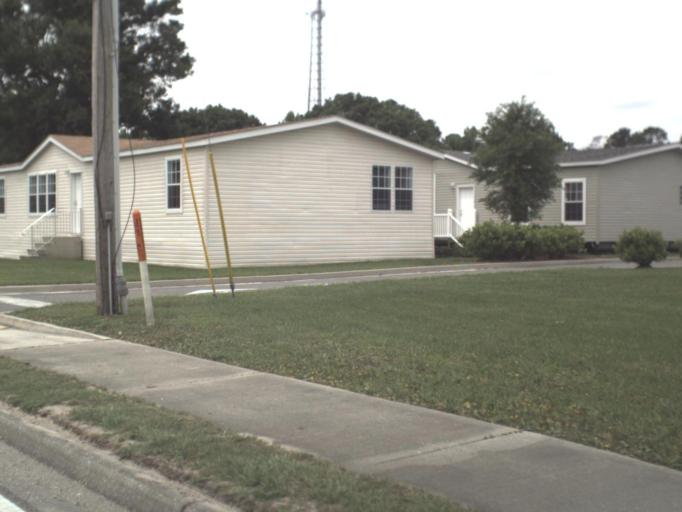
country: US
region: Florida
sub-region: Clay County
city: Middleburg
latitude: 30.0794
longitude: -81.8624
